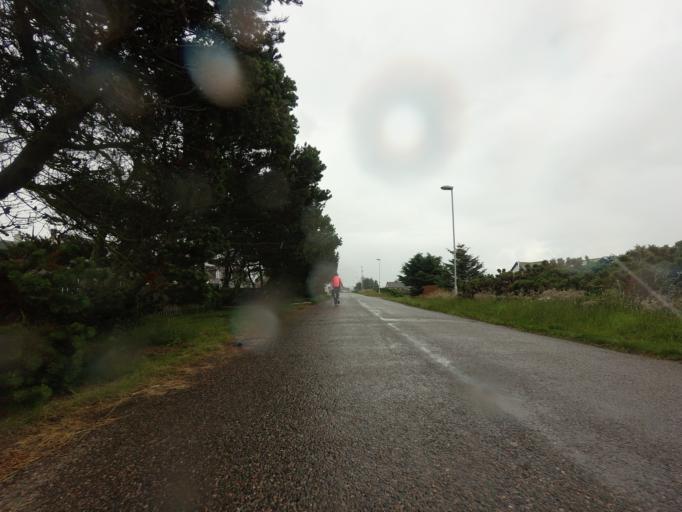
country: GB
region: Scotland
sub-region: Moray
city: Fochabers
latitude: 57.6727
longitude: -3.0872
